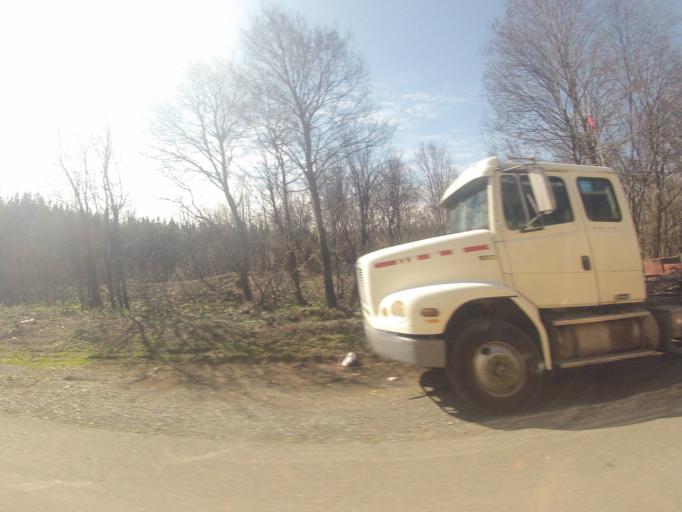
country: CL
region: Araucania
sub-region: Provincia de Malleco
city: Victoria
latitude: -38.1515
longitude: -72.3063
